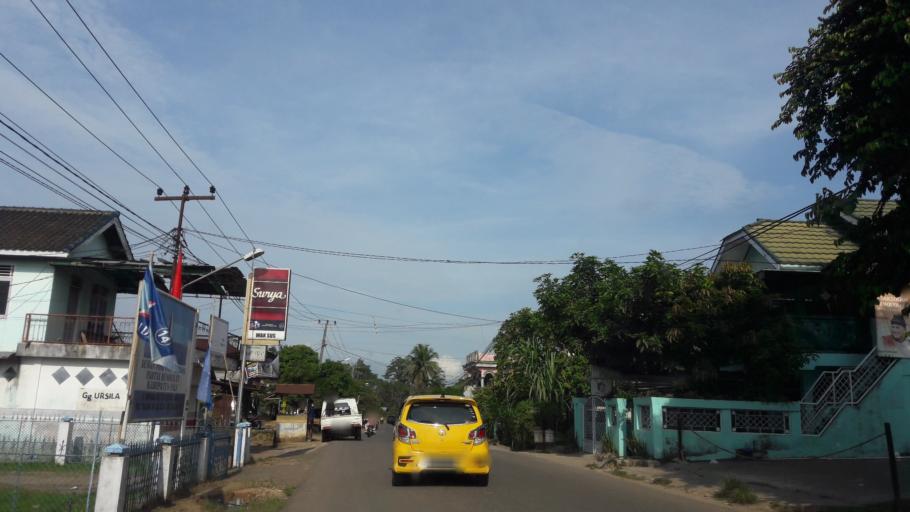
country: ID
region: South Sumatra
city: Gunungmegang Dalam
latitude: -3.2832
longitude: 103.8329
